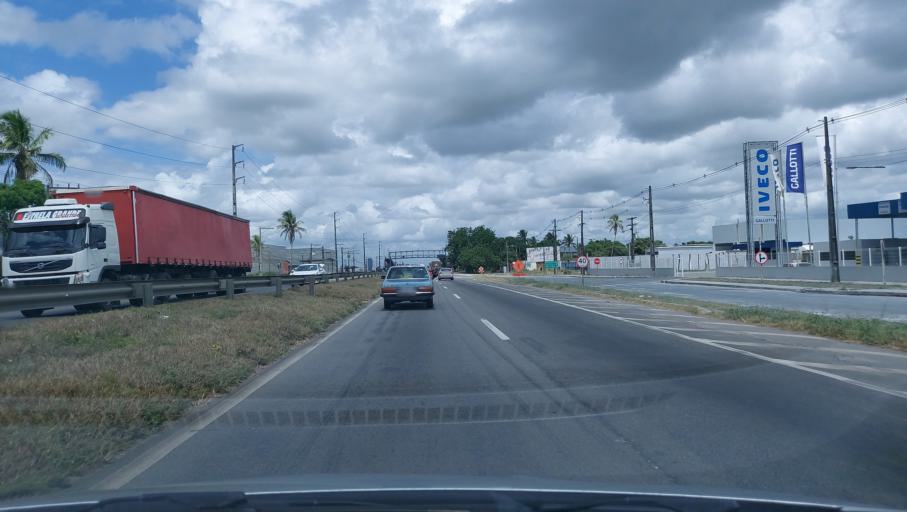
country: BR
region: Bahia
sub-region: Conceicao Do Jacuipe
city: Conceicao do Jacuipe
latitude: -12.3332
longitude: -38.8550
